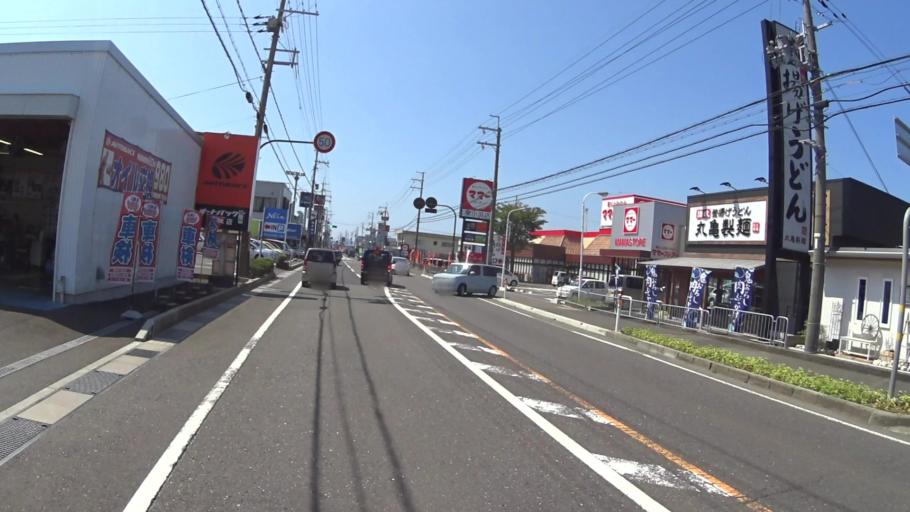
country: JP
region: Fukui
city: Obama
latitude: 35.4819
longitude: 135.7786
